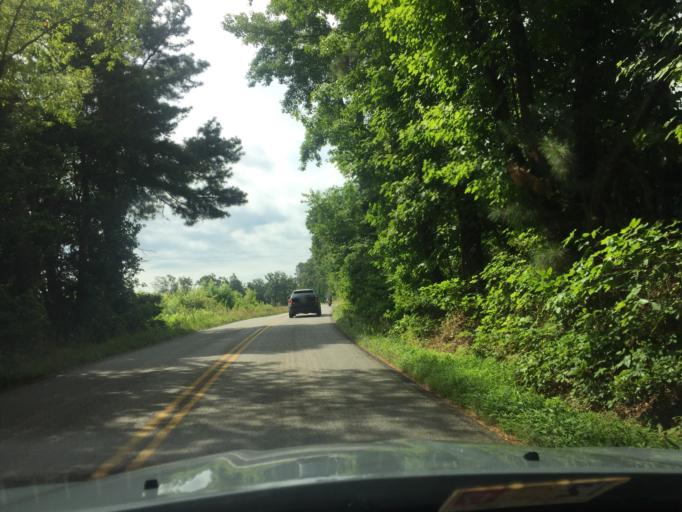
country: US
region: Virginia
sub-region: Charles City County
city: Charles City
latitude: 37.3857
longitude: -77.0111
